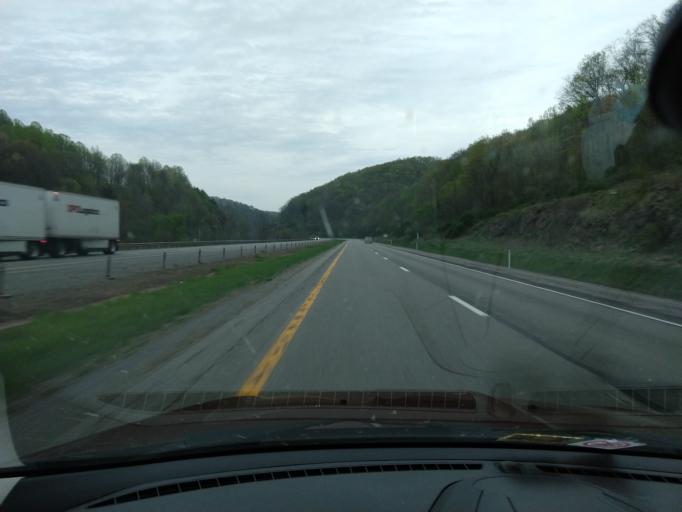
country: US
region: West Virginia
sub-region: Lewis County
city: Weston
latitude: 38.9848
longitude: -80.5070
